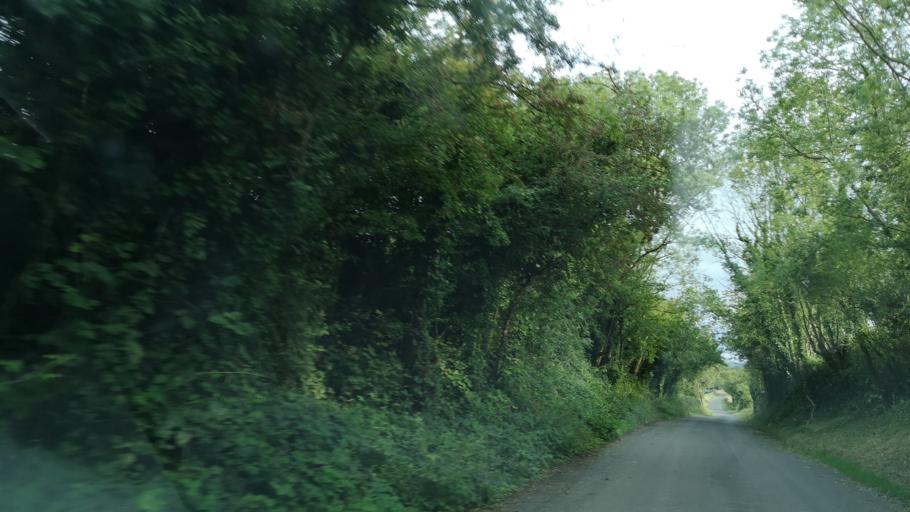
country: IE
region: Leinster
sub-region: Uibh Fhaili
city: Ferbane
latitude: 53.1840
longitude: -7.7271
